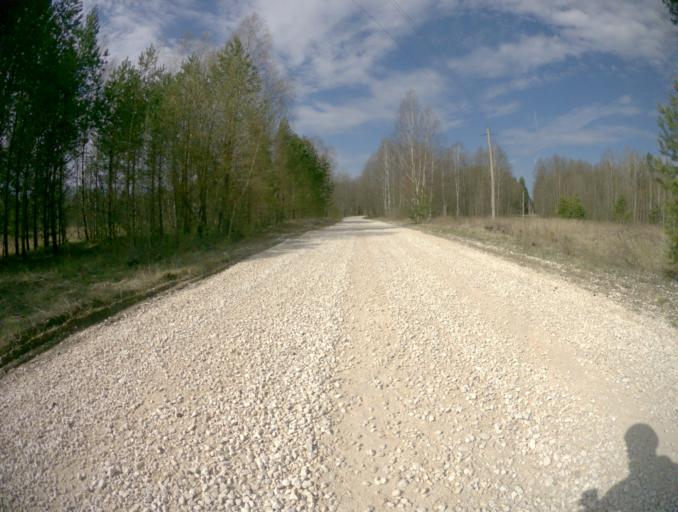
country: RU
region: Vladimir
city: Mezinovskiy
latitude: 55.4924
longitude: 40.3358
